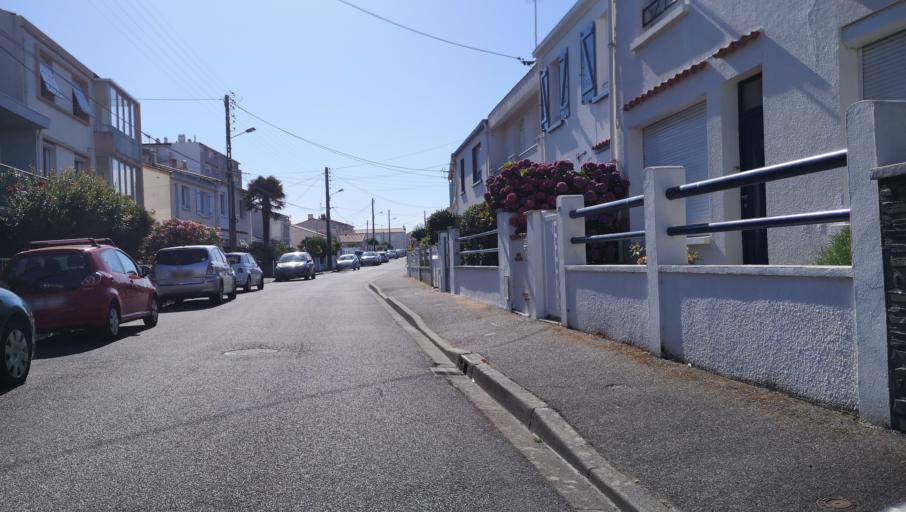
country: FR
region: Pays de la Loire
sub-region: Departement de la Vendee
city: Les Sables-d'Olonne
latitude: 46.4903
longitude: -1.7626
